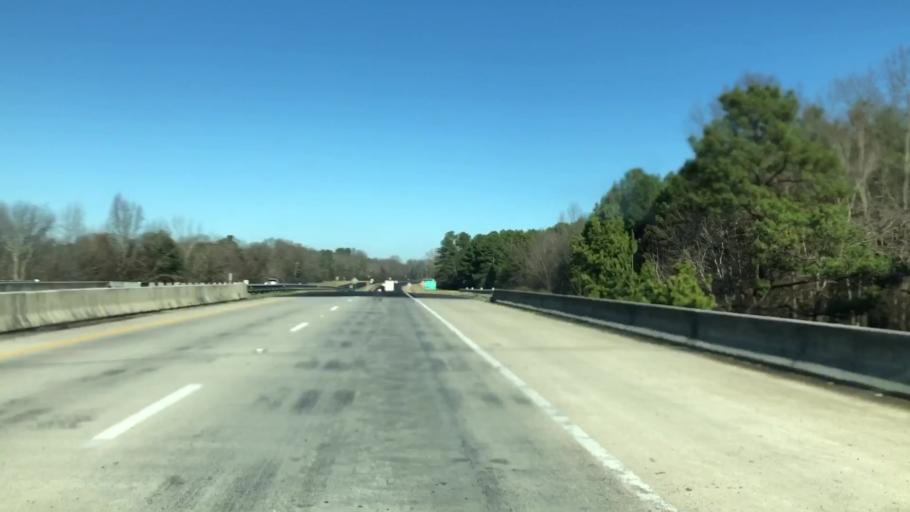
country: US
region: Alabama
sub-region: Limestone County
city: Ardmore
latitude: 34.9063
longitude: -86.9067
